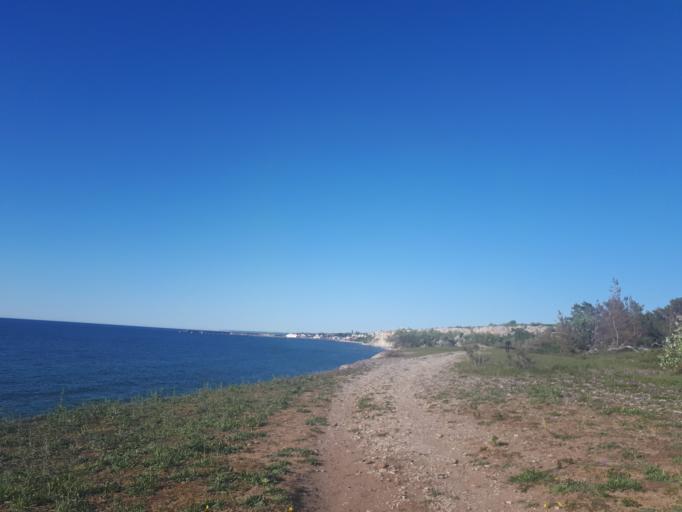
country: SE
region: Gotland
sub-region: Gotland
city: Vibble
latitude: 57.6149
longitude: 18.2524
